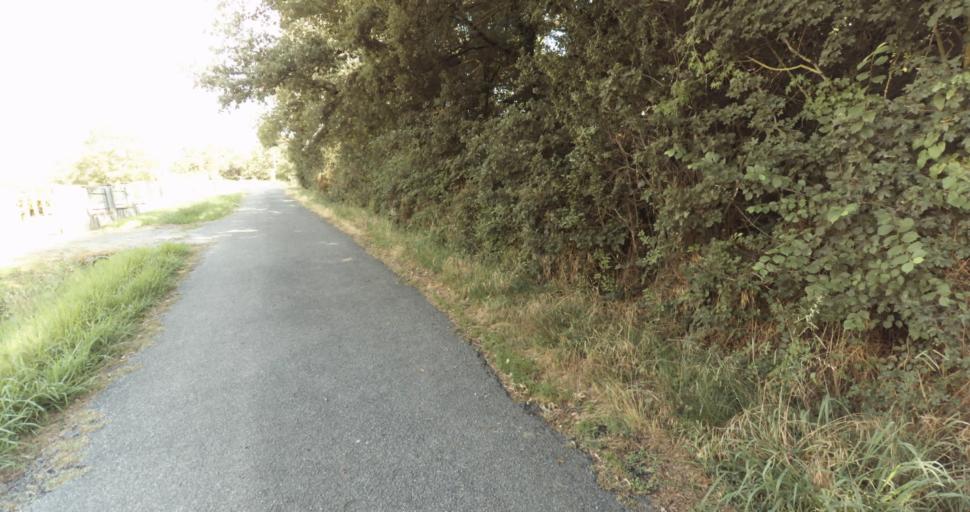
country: FR
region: Midi-Pyrenees
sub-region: Departement de la Haute-Garonne
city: Fonsorbes
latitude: 43.5602
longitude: 1.2329
